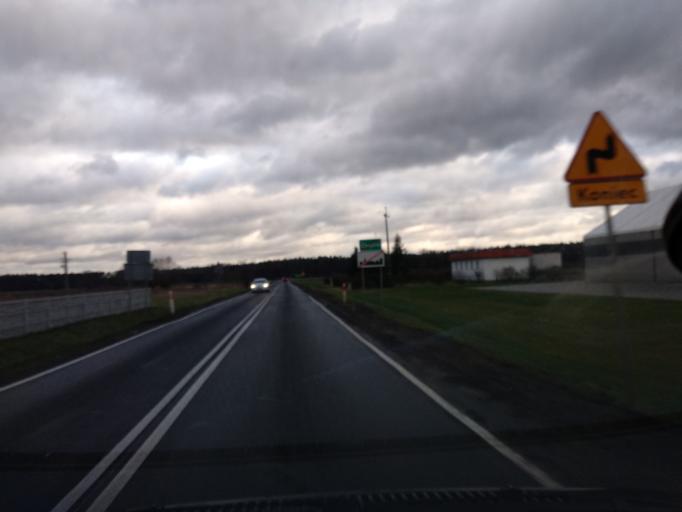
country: PL
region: Lower Silesian Voivodeship
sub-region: Powiat olesnicki
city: Miedzyborz
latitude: 51.4427
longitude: 17.7029
